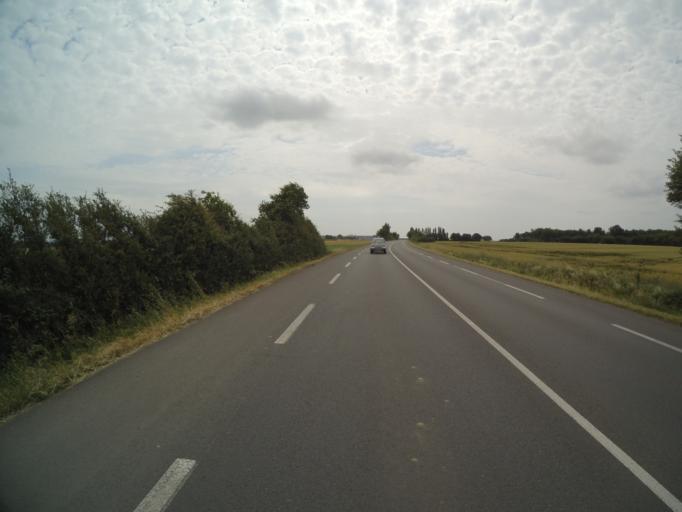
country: FR
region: Pays de la Loire
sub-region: Departement de la Vendee
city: Chavagnes-en-Paillers
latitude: 46.9200
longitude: -1.2467
